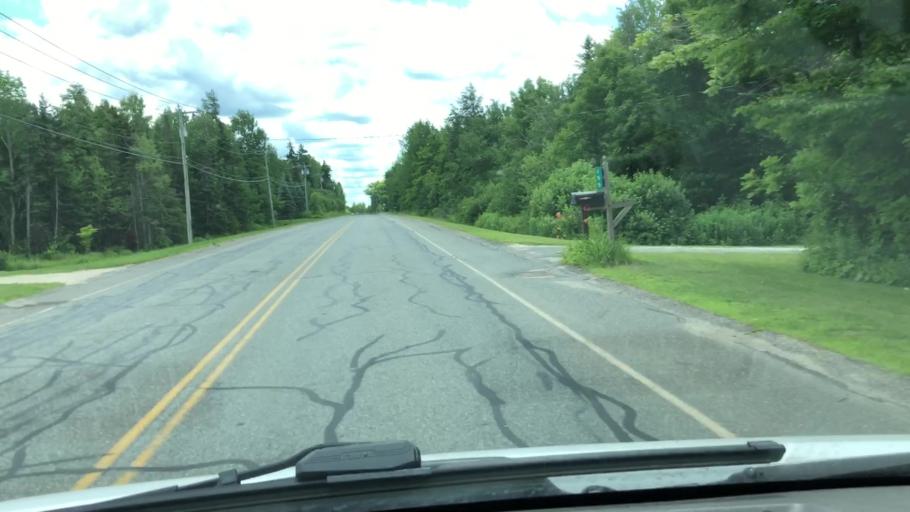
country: US
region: Massachusetts
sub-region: Berkshire County
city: Adams
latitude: 42.5607
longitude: -73.0448
